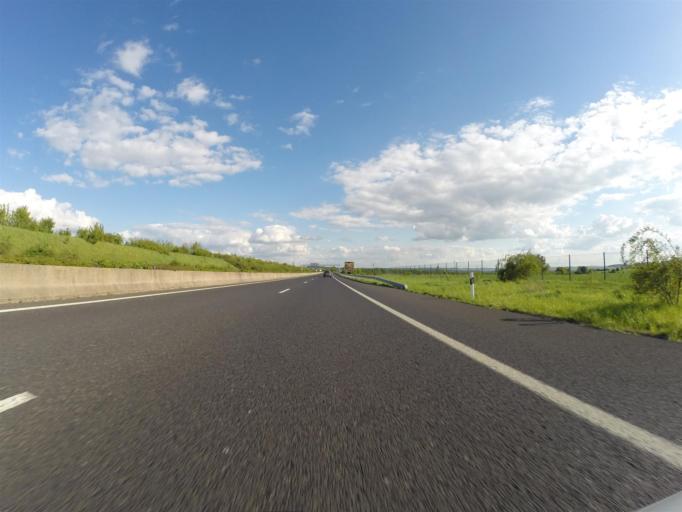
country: LU
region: Grevenmacher
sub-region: Canton de Remich
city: Mondorf-les-Bains
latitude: 49.5057
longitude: 6.3035
